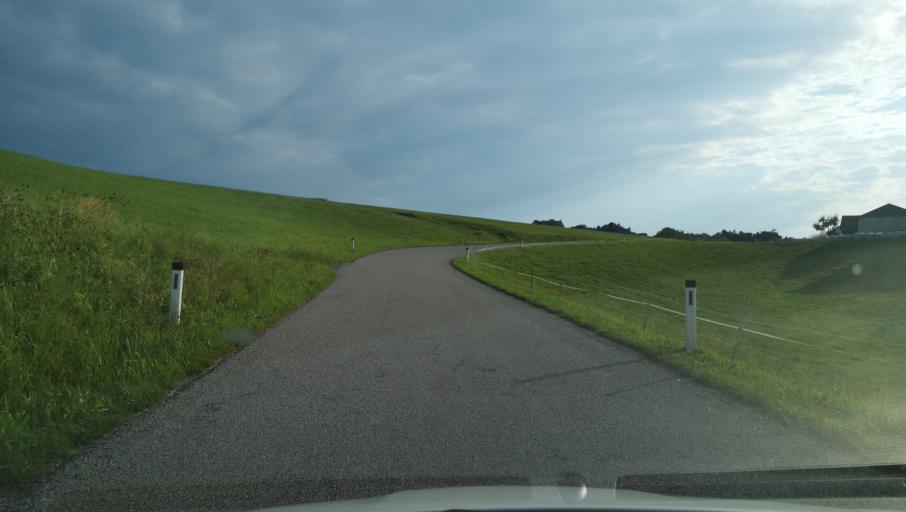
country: AT
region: Lower Austria
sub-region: Politischer Bezirk Amstetten
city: Sankt Georgen am Ybbsfelde
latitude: 48.1587
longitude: 14.9548
